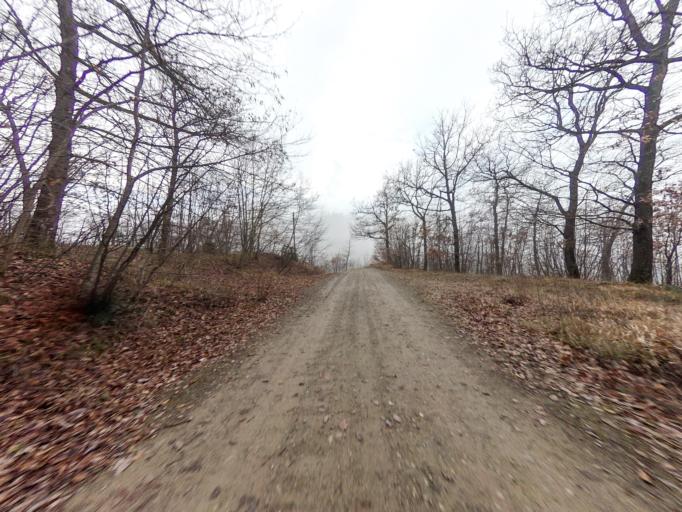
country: IT
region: Emilia-Romagna
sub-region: Provincia di Bologna
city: Monterenzio
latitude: 44.3260
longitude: 11.3488
